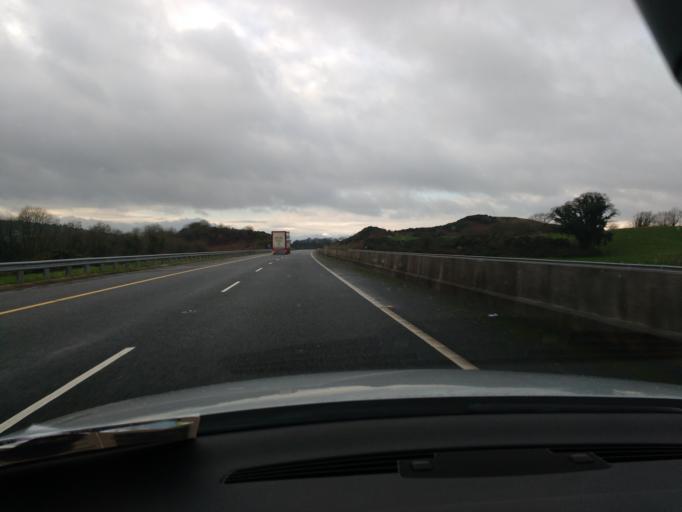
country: IE
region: Munster
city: Ballina
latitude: 52.7924
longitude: -8.3407
